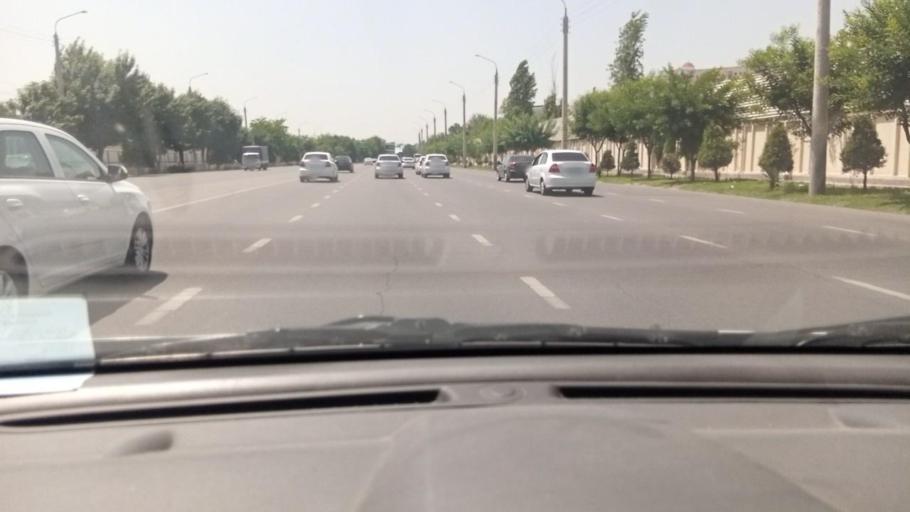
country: UZ
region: Toshkent Shahri
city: Tashkent
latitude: 41.2743
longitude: 69.2692
